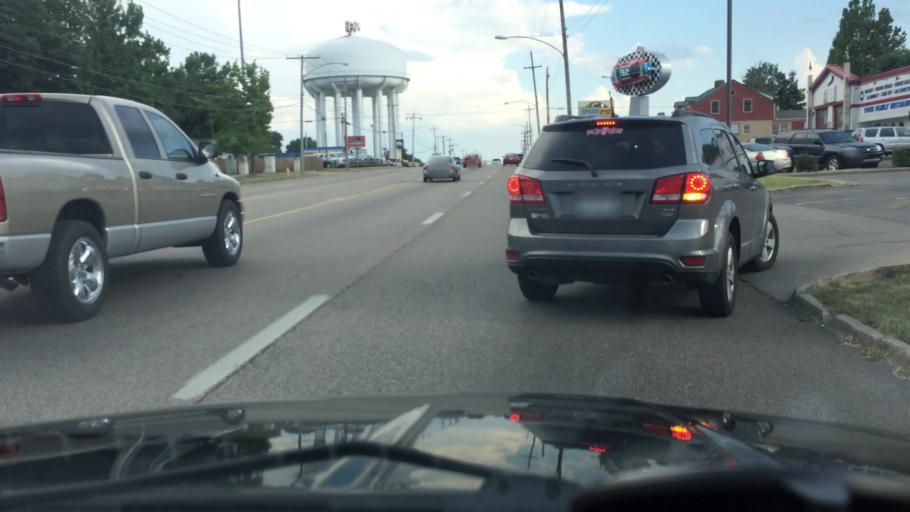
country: US
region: Missouri
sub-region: Greene County
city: Springfield
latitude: 37.2028
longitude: -93.2620
